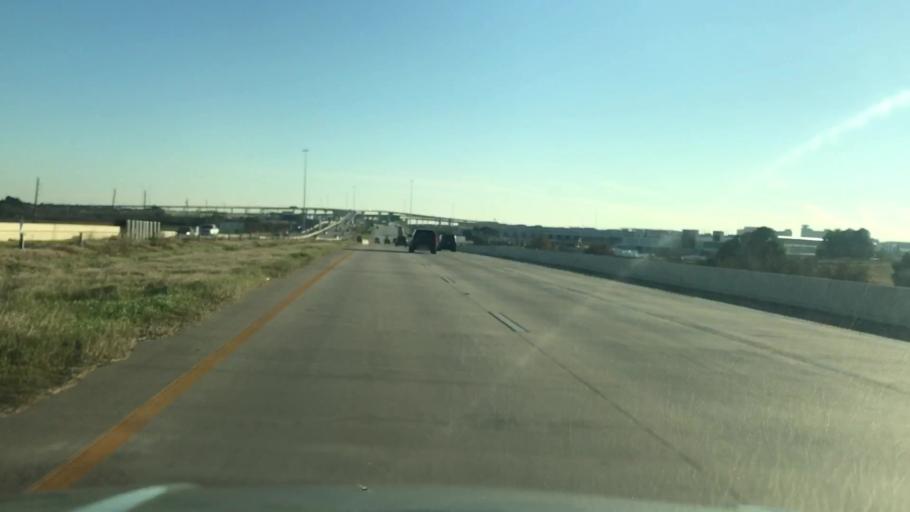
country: US
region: Texas
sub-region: Harris County
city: Katy
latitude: 29.8012
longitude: -95.7757
